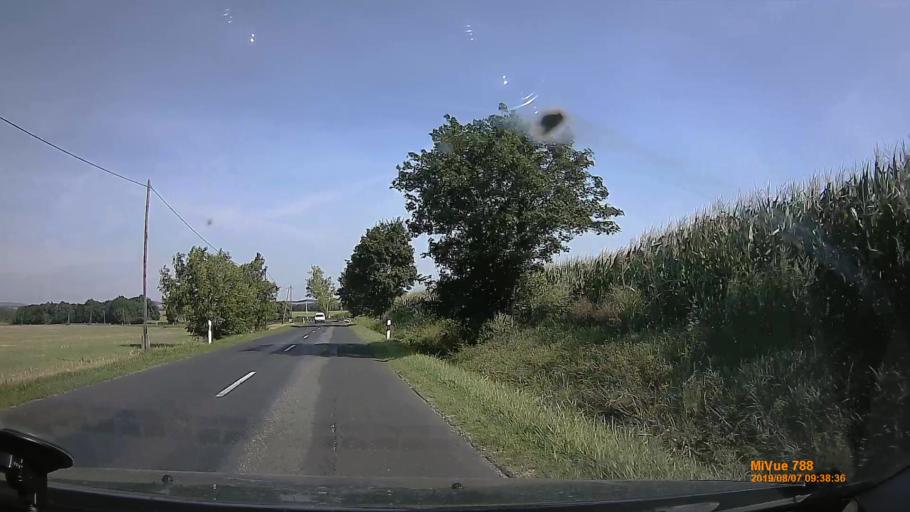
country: HU
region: Zala
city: Pacsa
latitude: 46.7272
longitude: 17.0882
